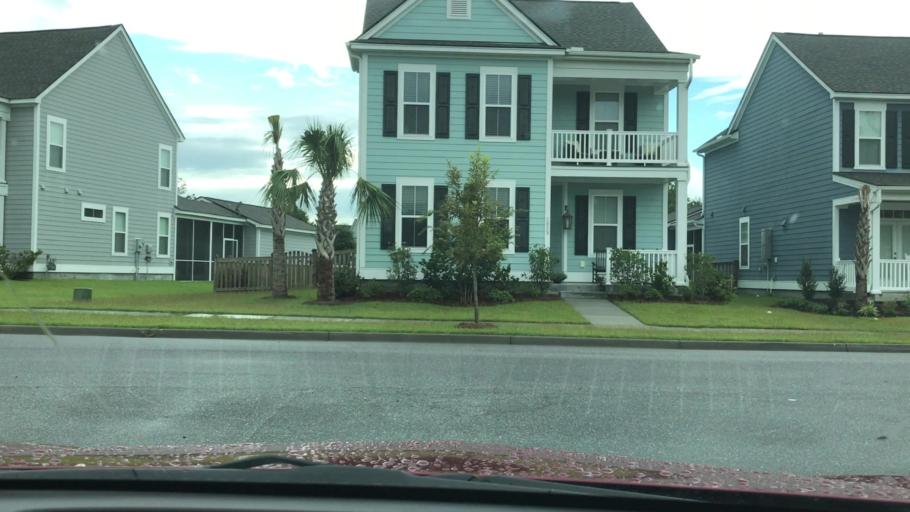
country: US
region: South Carolina
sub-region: Charleston County
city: Shell Point
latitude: 32.8074
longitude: -80.0705
